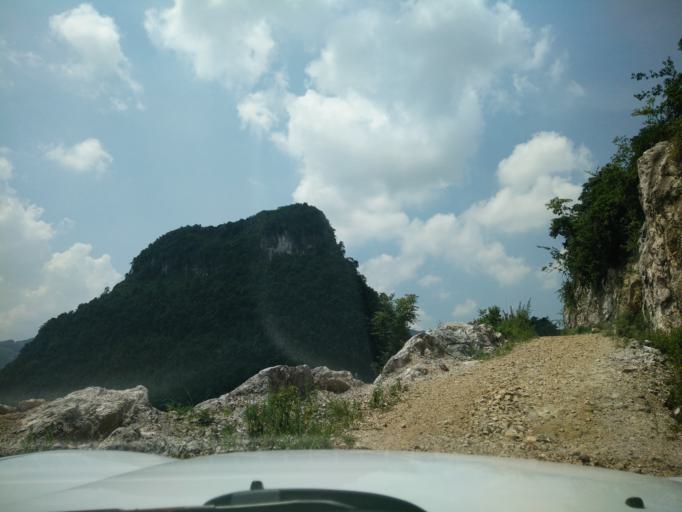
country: CN
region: Guangxi Zhuangzu Zizhiqu
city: Xinzhou
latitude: 25.0085
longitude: 105.7046
